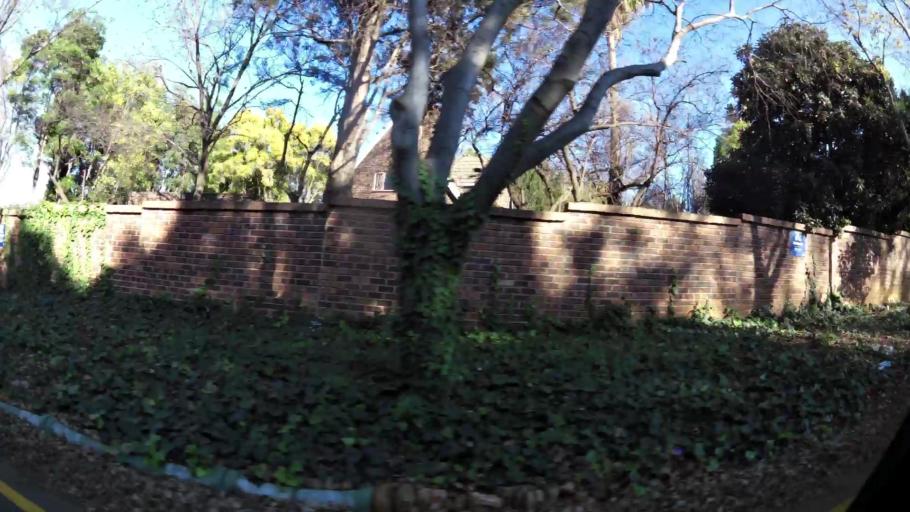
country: ZA
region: Gauteng
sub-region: City of Johannesburg Metropolitan Municipality
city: Midrand
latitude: -26.0295
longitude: 28.0511
